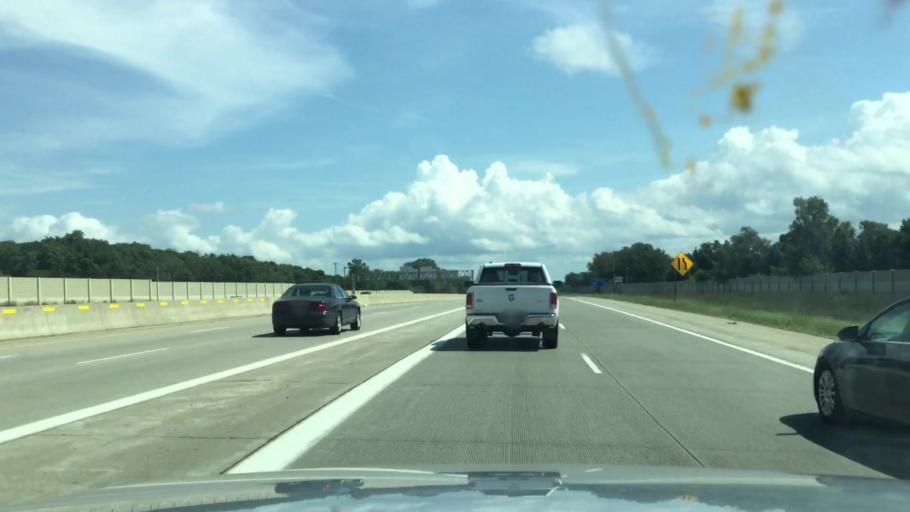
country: US
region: Michigan
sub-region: Kalamazoo County
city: Portage
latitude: 42.2378
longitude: -85.6328
